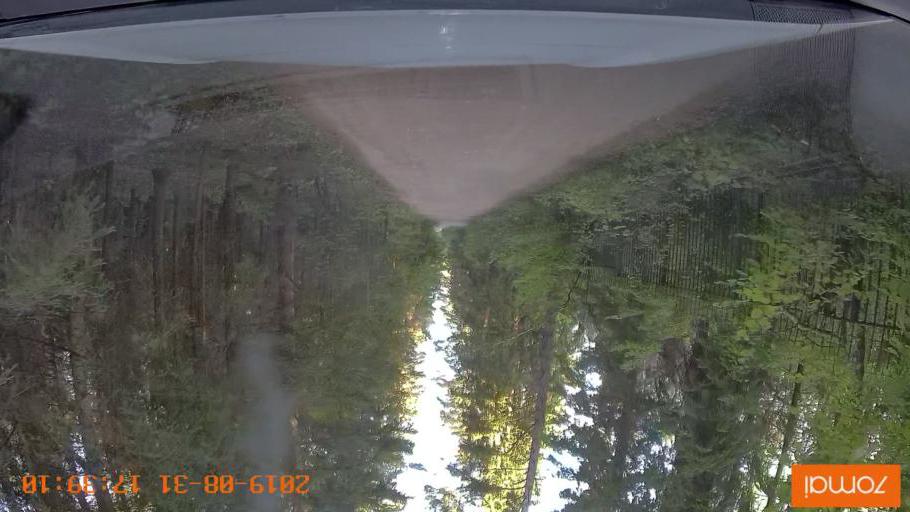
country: RU
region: Kaluga
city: Detchino
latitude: 54.8167
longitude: 36.3625
